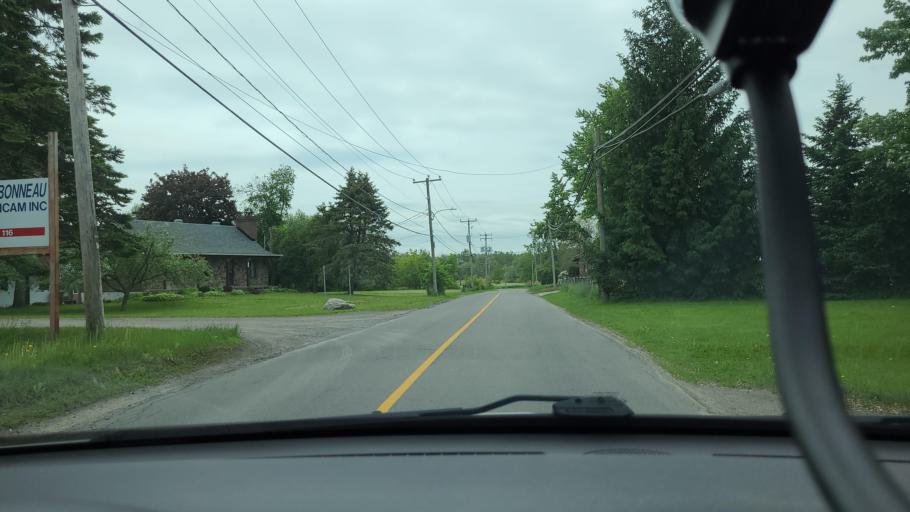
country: CA
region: Quebec
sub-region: Laurentides
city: Rosemere
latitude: 45.6321
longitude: -73.7692
